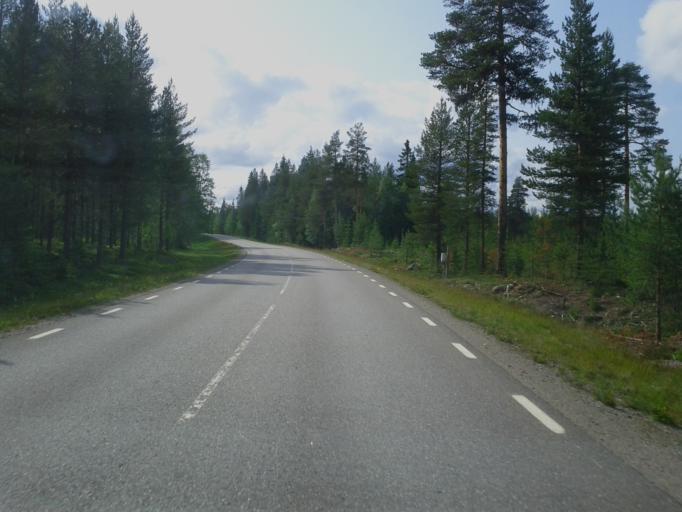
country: SE
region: Vaesterbotten
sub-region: Mala Kommun
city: Mala
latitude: 65.2317
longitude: 18.5684
